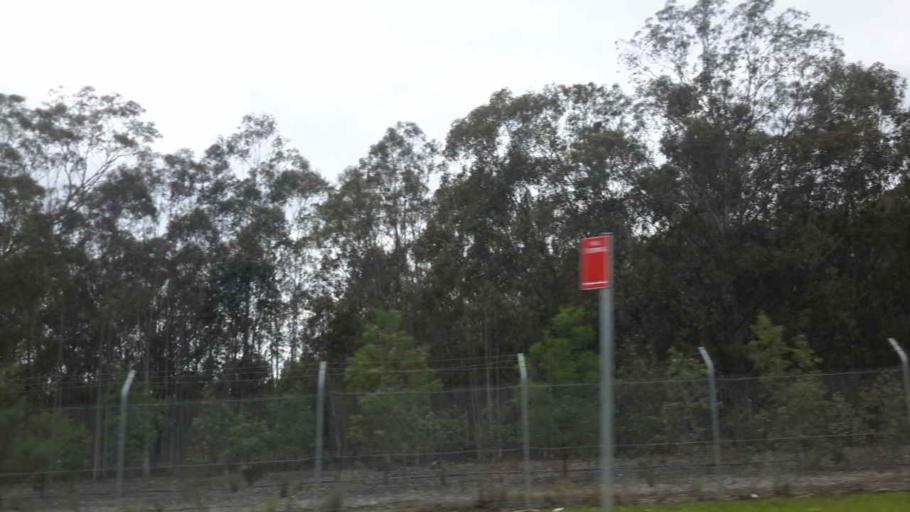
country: AU
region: New South Wales
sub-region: Penrith Municipality
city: Werrington Downs
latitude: -33.7295
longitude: 150.7195
